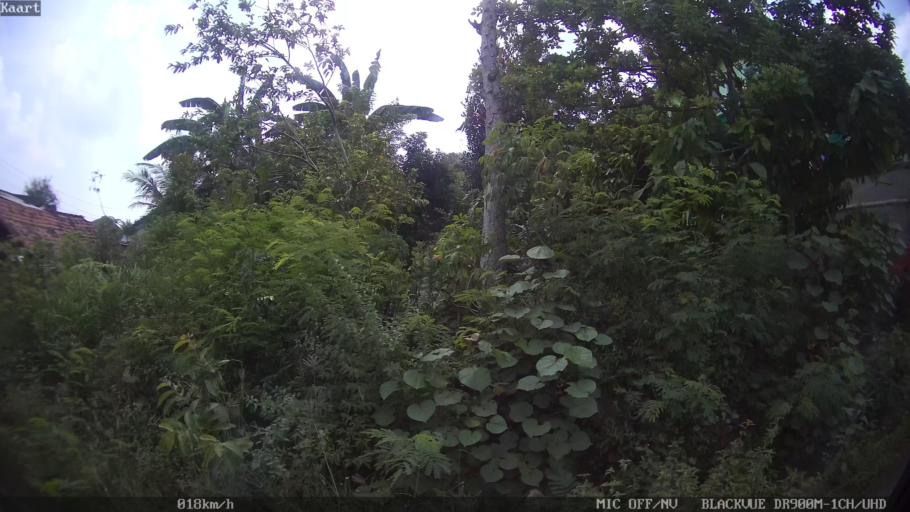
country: ID
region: Lampung
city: Pringsewu
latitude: -5.3586
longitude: 104.9630
